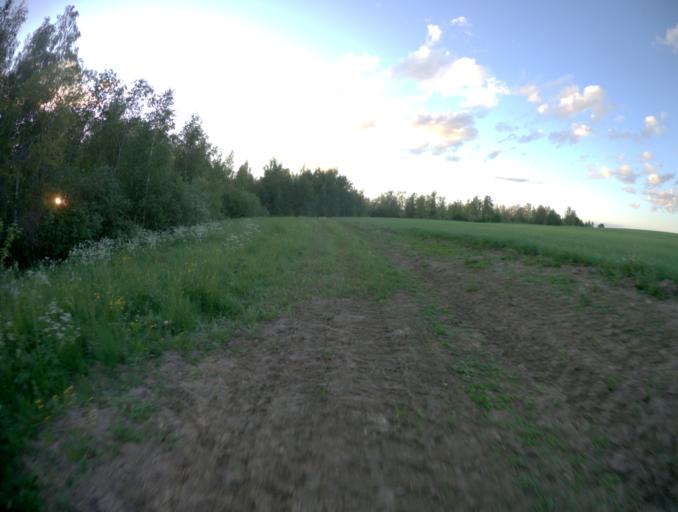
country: RU
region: Ivanovo
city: Gavrilov Posad
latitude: 56.5378
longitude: 40.1954
